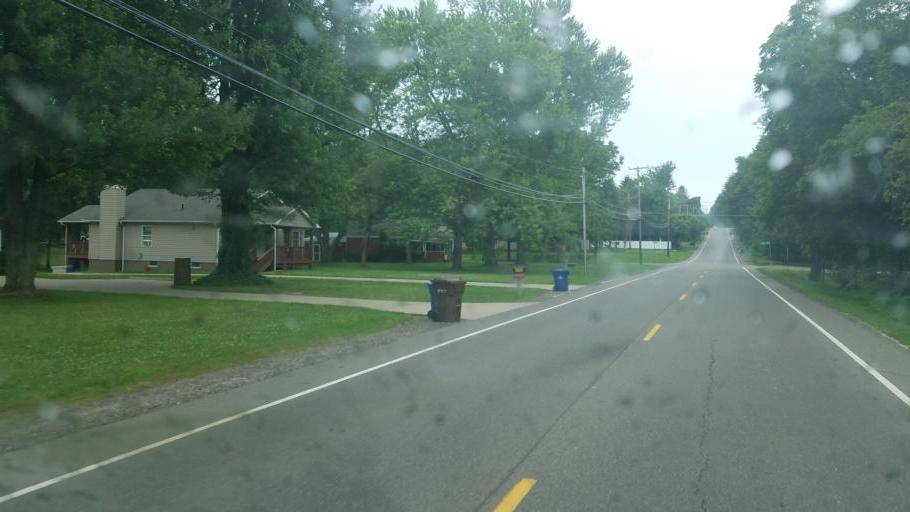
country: US
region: Ohio
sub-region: Summit County
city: Manchester
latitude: 40.9753
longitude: -81.5632
